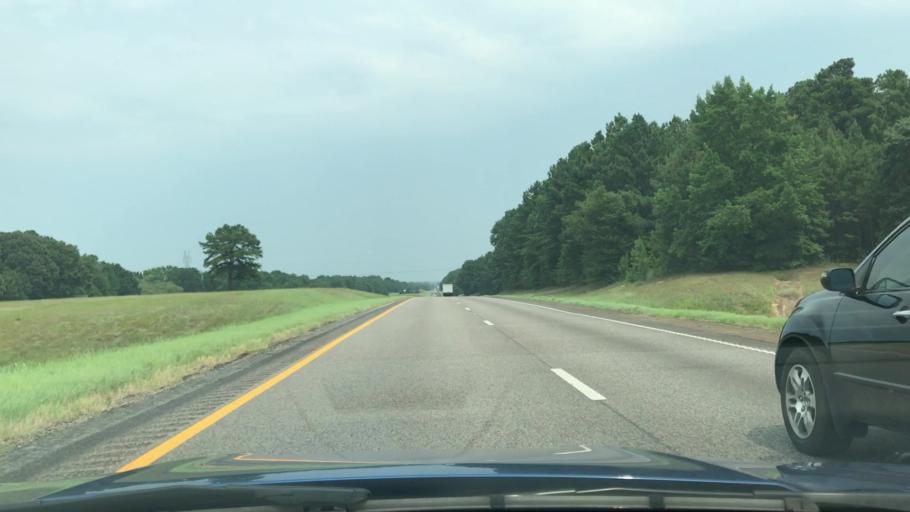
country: US
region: Texas
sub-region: Smith County
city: Tyler
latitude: 32.4520
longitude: -95.2612
